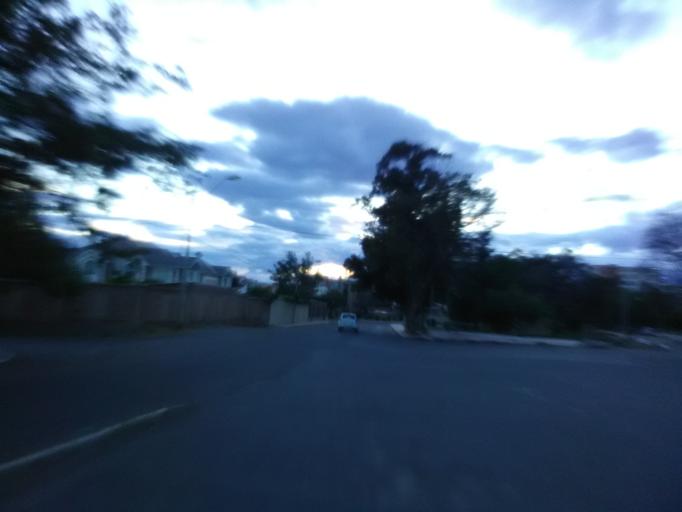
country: BO
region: Cochabamba
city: Cochabamba
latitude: -17.3749
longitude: -66.1444
